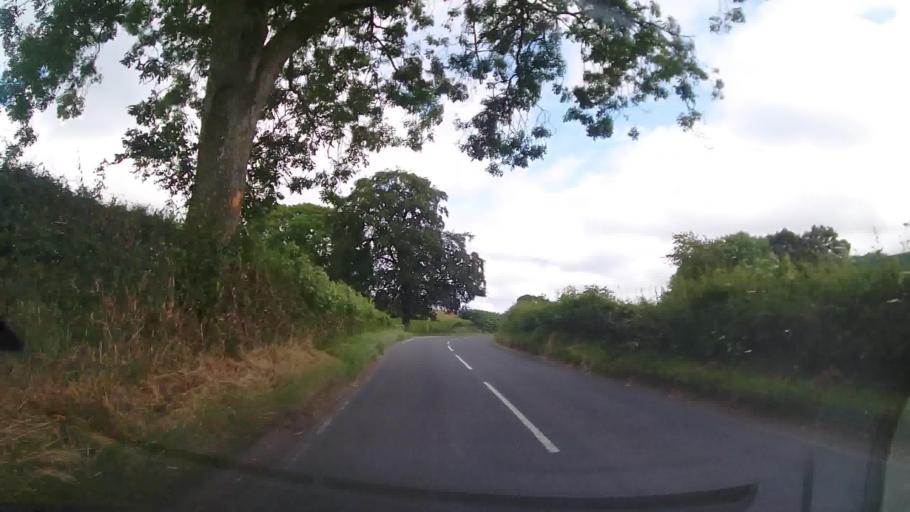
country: GB
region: Wales
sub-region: Sir Powys
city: Llanrhaeadr-ym-Mochnant
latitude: 52.8139
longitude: -3.2698
